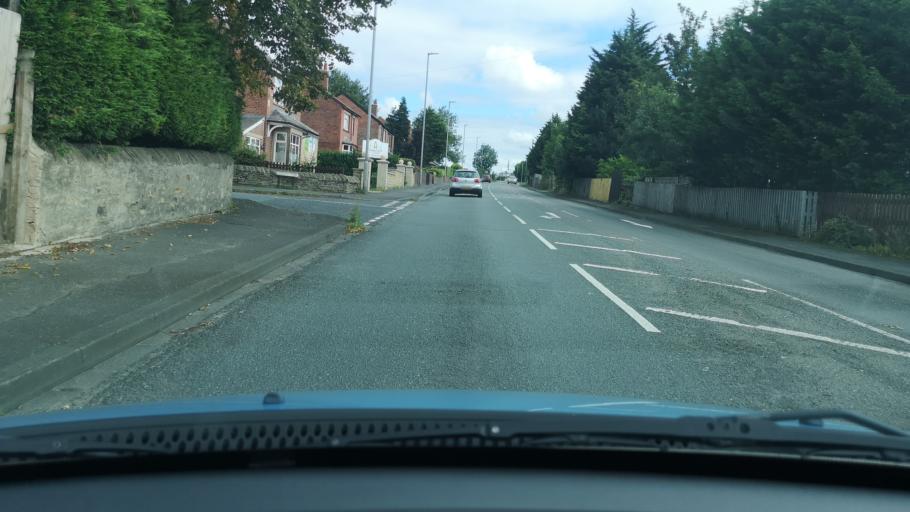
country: GB
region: England
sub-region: Kirklees
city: Heckmondwike
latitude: 53.7174
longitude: -1.6764
